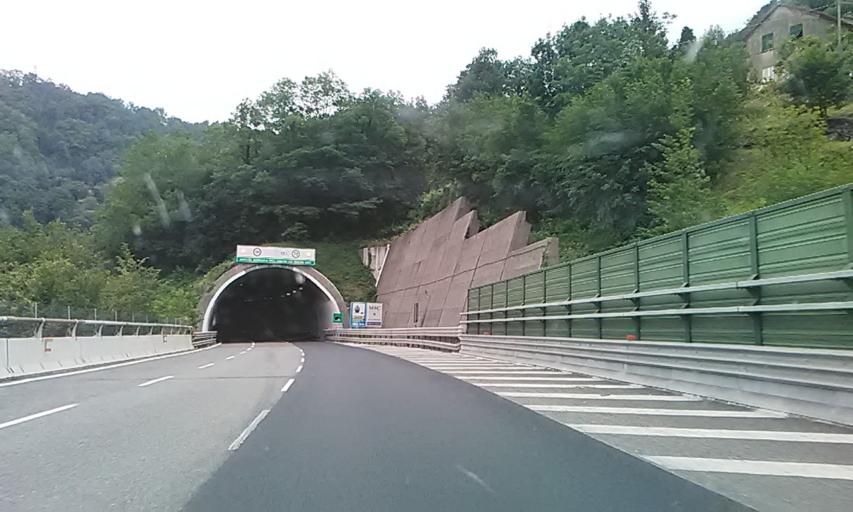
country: IT
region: Liguria
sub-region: Provincia di Genova
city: Mele
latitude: 44.4462
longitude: 8.7151
